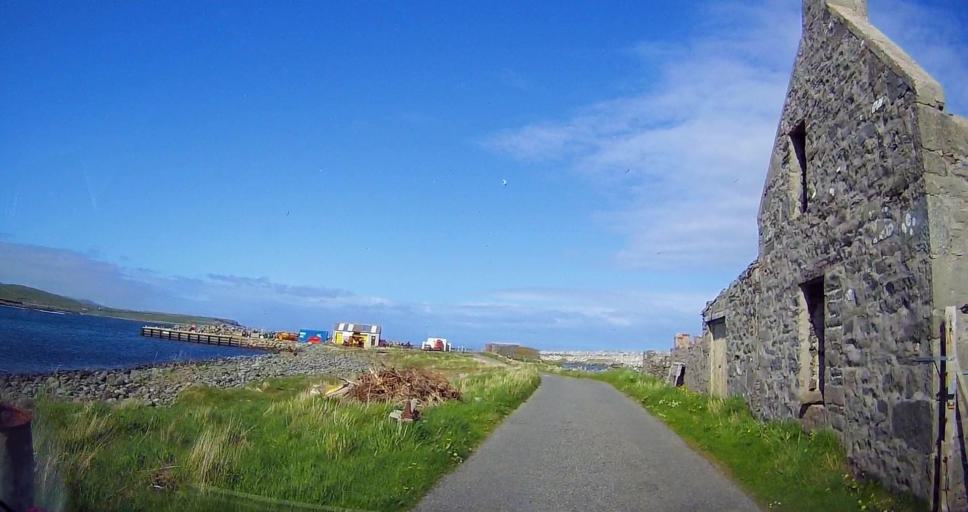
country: GB
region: Scotland
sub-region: Shetland Islands
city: Sandwick
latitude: 59.8730
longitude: -1.2788
